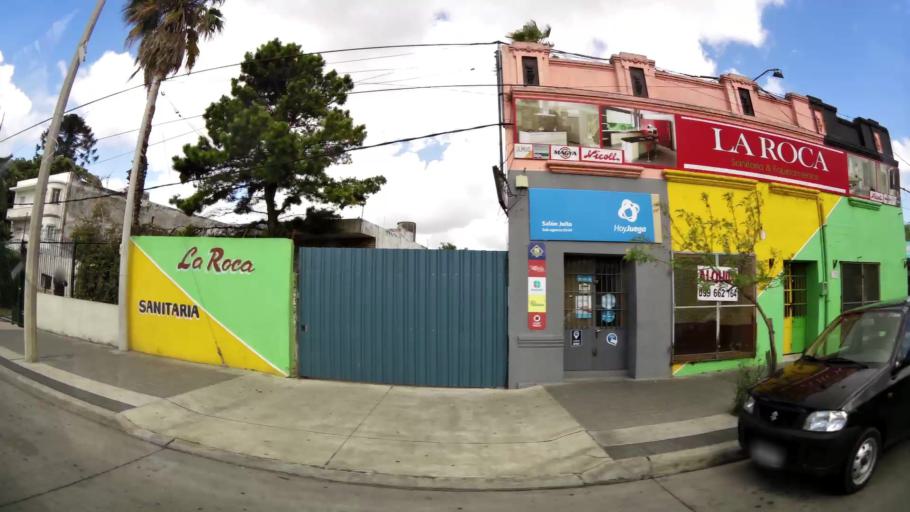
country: UY
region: Montevideo
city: Montevideo
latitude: -34.8513
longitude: -56.2240
